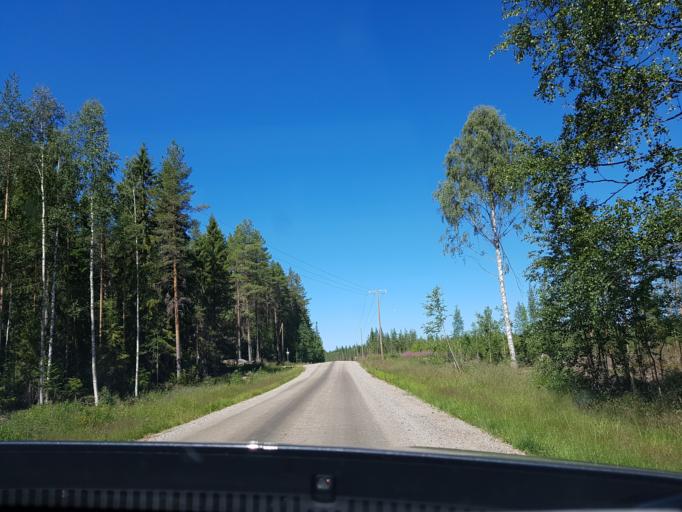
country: FI
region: Kainuu
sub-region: Kehys-Kainuu
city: Kuhmo
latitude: 64.1798
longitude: 29.6030
